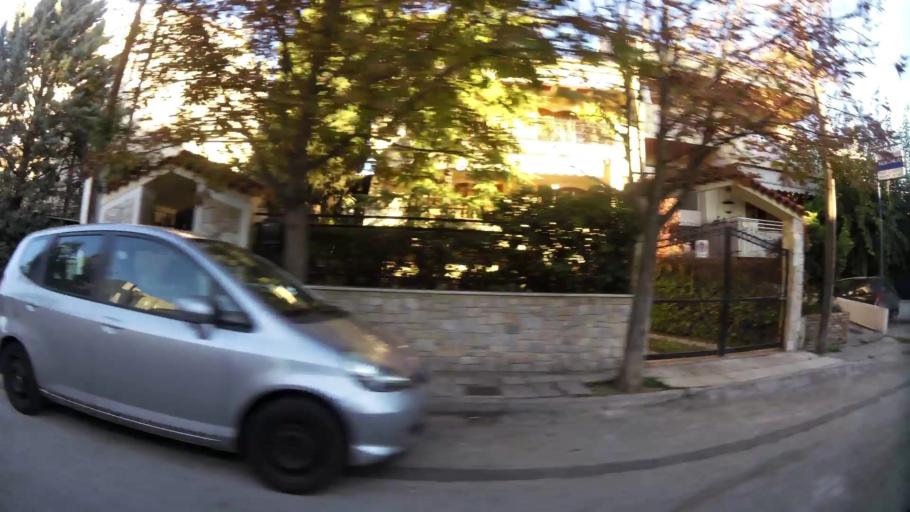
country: GR
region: Attica
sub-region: Nomarchia Athinas
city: Kifisia
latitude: 38.0725
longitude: 23.8041
